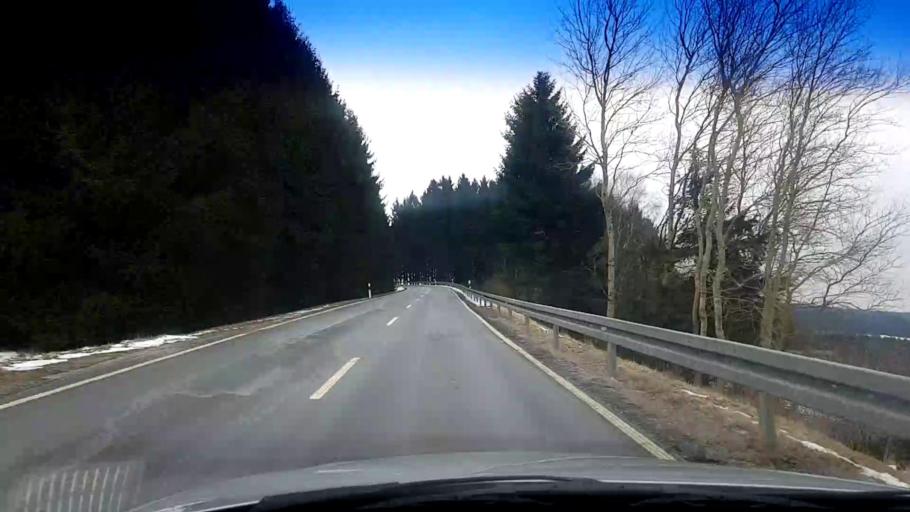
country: DE
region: Bavaria
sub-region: Upper Franconia
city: Gefrees
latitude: 50.0821
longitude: 11.7519
